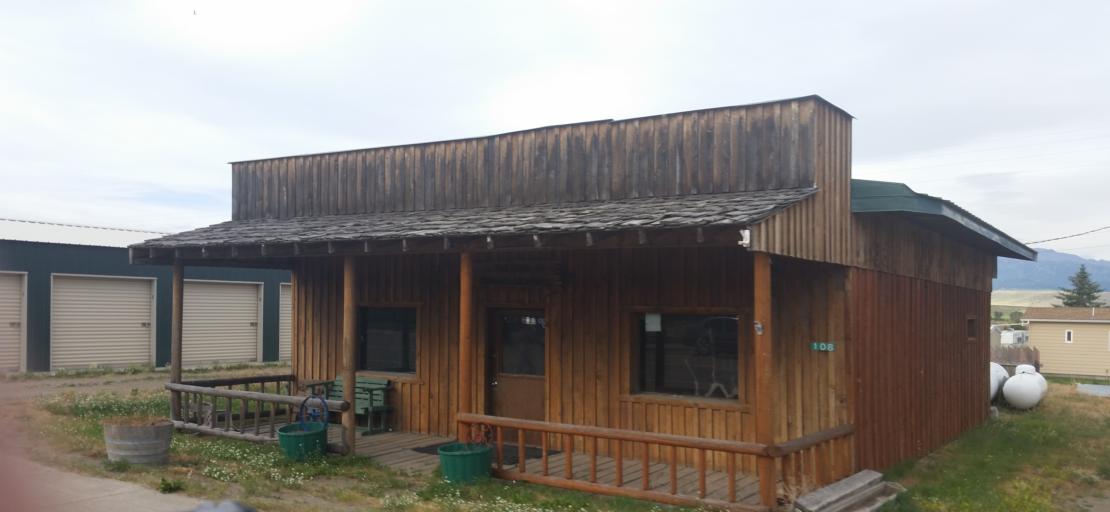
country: US
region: Montana
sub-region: Park County
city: Livingston
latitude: 45.9941
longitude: -110.6604
